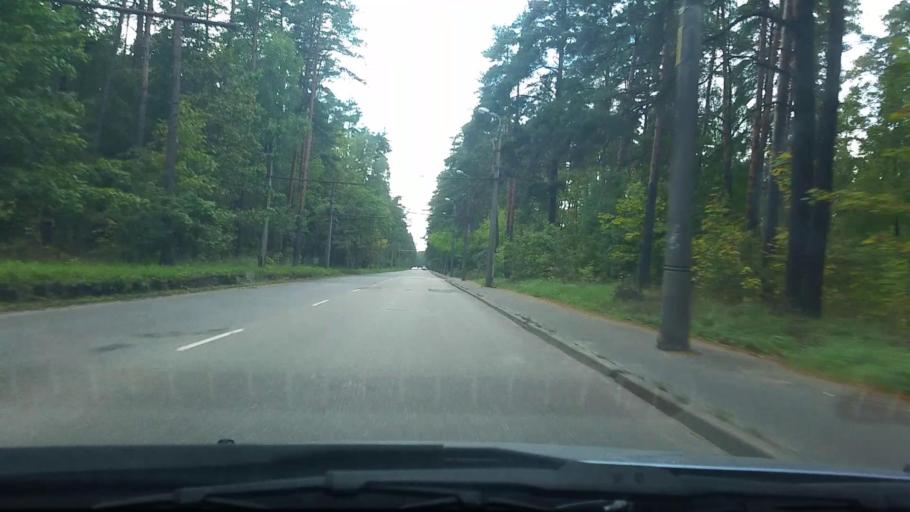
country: LV
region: Stopini
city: Ulbroka
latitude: 56.9619
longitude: 24.2214
